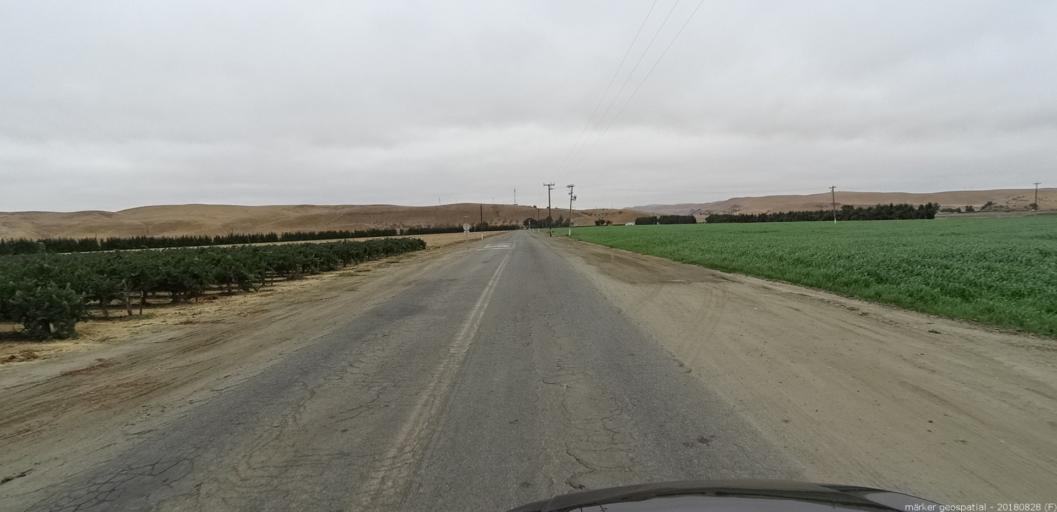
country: US
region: California
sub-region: San Luis Obispo County
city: Lake Nacimiento
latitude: 36.0206
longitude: -120.9007
